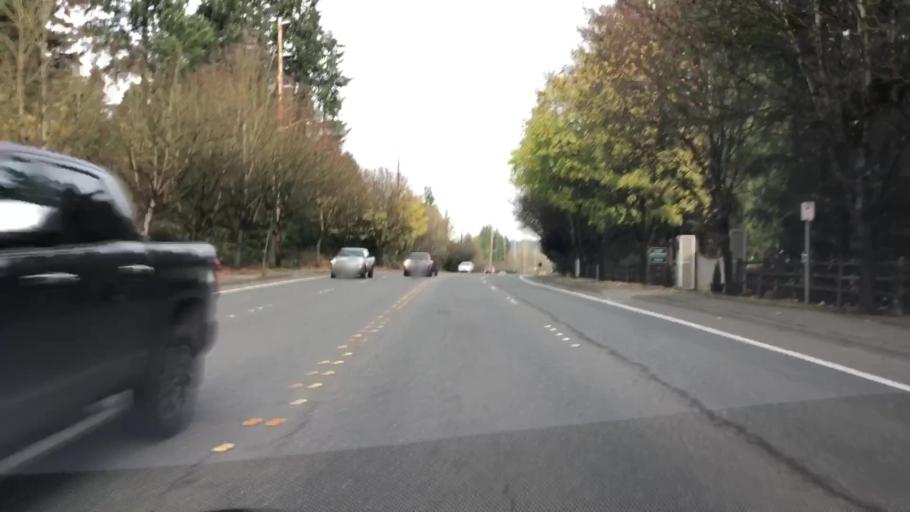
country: US
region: Washington
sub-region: King County
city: Redmond
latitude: 47.6951
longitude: -122.0931
